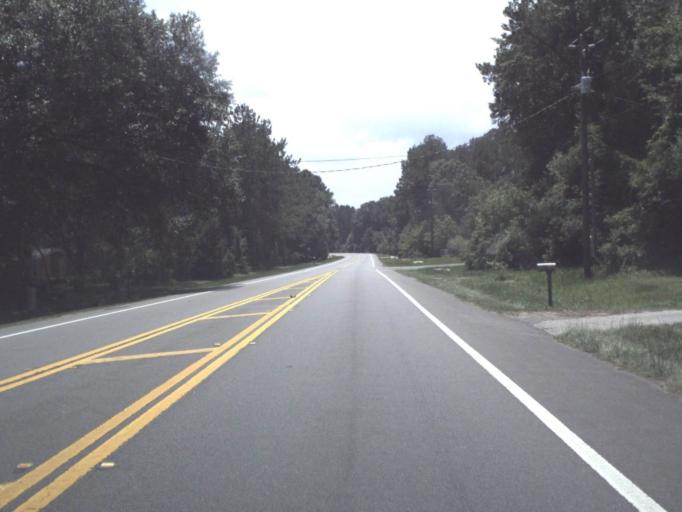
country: US
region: Florida
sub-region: Nassau County
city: Nassau Village-Ratliff
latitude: 30.5244
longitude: -81.7693
